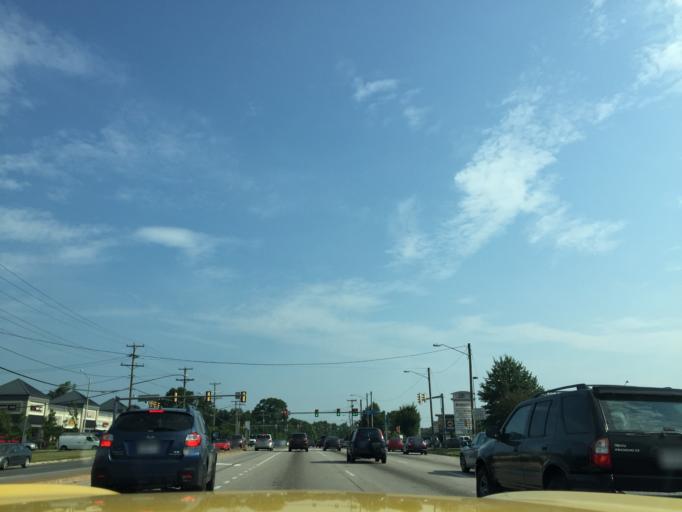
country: US
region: Virginia
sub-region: Fairfax County
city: Hybla Valley
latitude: 38.7503
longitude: -77.0832
